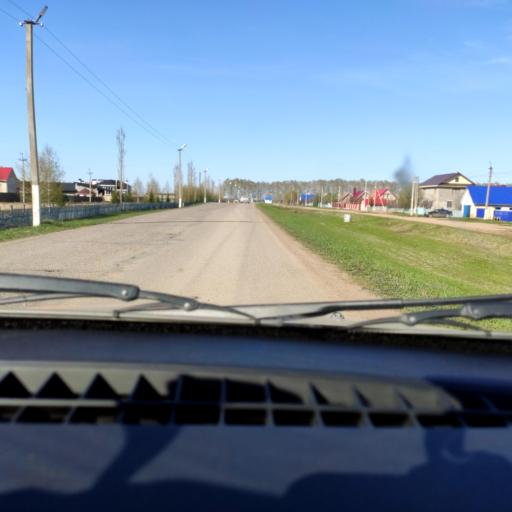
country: RU
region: Bashkortostan
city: Kabakovo
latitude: 54.6012
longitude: 56.1840
